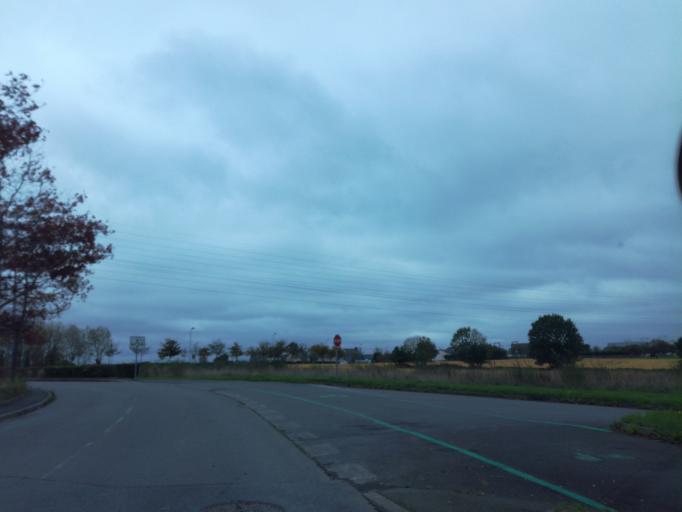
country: FR
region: Brittany
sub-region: Departement d'Ille-et-Vilaine
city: La Richardais
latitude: 48.6122
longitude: -2.0471
